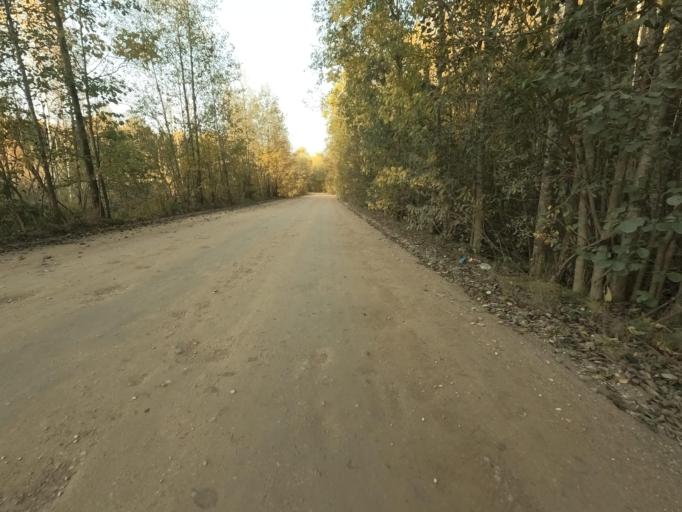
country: RU
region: Leningrad
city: Lyuban'
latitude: 58.9907
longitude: 31.1039
